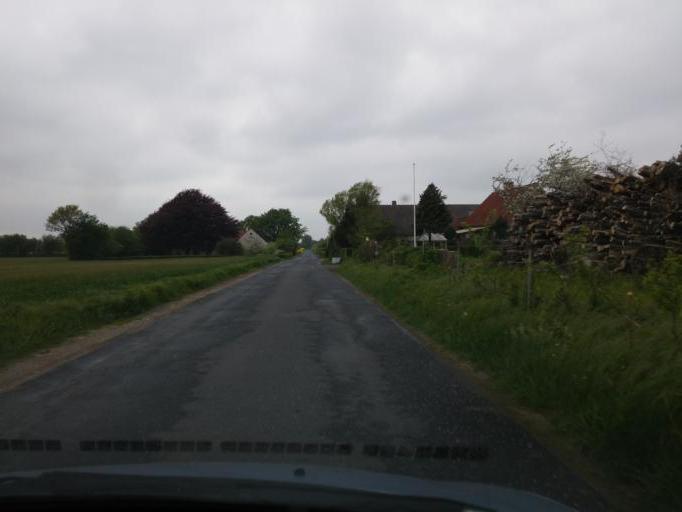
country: DK
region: South Denmark
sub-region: Odense Kommune
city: Bullerup
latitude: 55.4148
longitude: 10.4950
